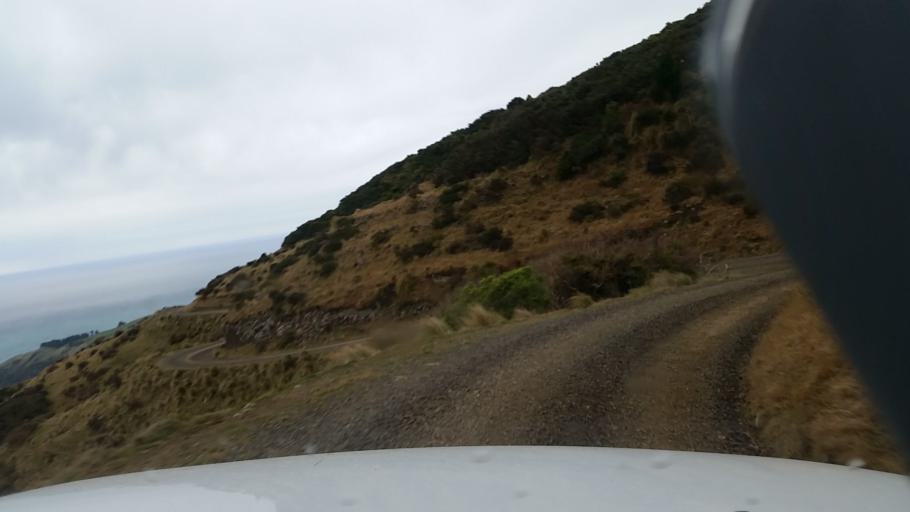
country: NZ
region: Canterbury
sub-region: Christchurch City
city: Christchurch
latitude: -43.8526
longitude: 172.8875
